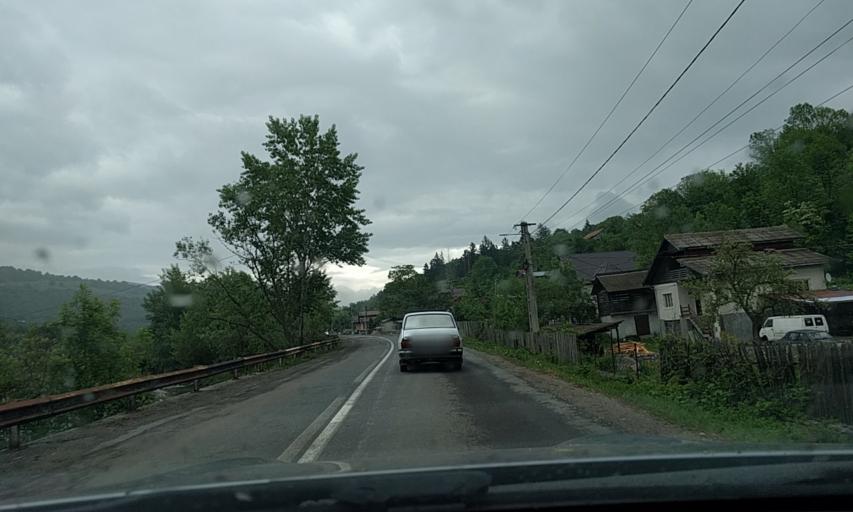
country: RO
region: Dambovita
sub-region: Comuna Moroeni
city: Glod
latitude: 45.2323
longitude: 25.4402
